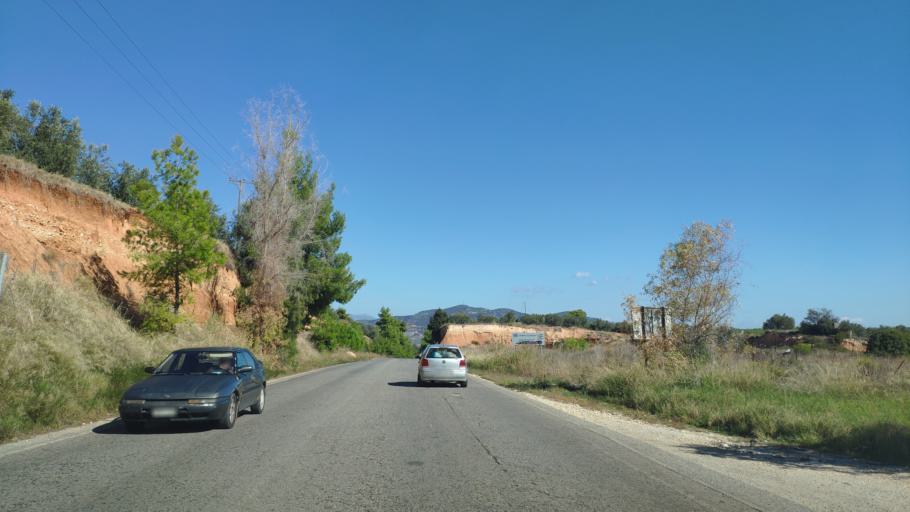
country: GR
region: Peloponnese
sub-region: Nomos Korinthias
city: Khiliomodhi
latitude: 37.8178
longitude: 22.8746
